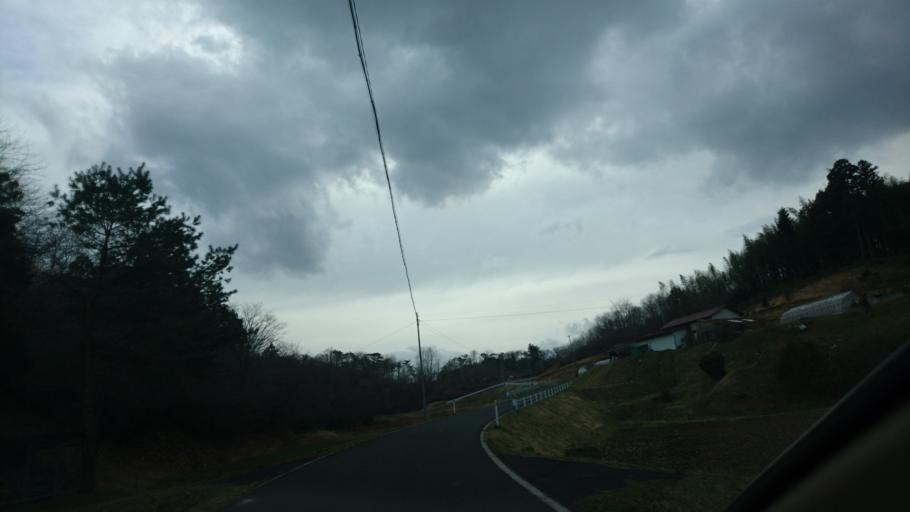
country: JP
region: Iwate
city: Ichinoseki
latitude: 38.8838
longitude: 141.1664
